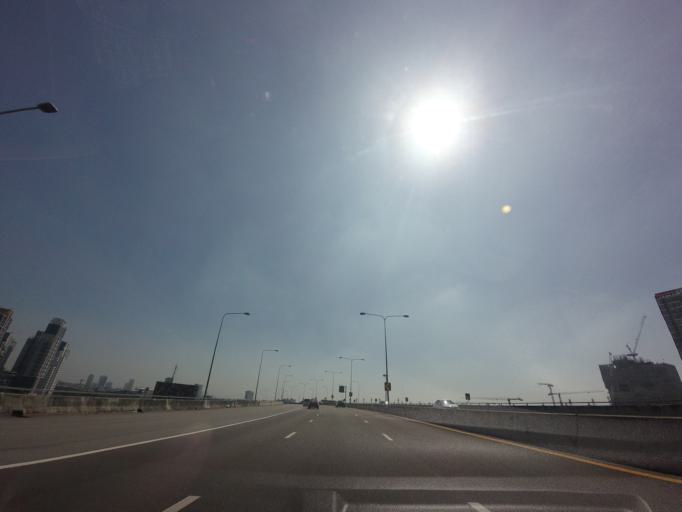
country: TH
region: Bangkok
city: Phra Khanong
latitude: 13.6740
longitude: 100.6060
